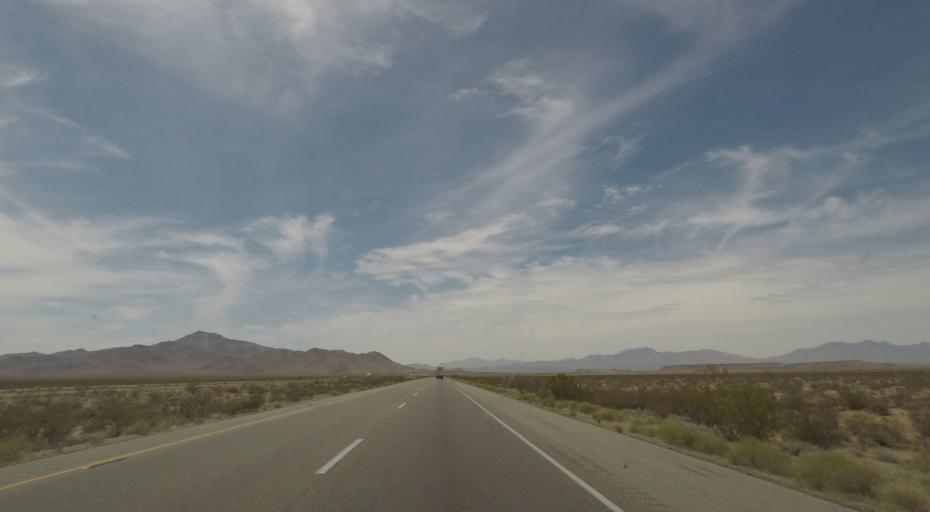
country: US
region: California
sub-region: San Bernardino County
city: Needles
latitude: 34.8043
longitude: -115.2817
